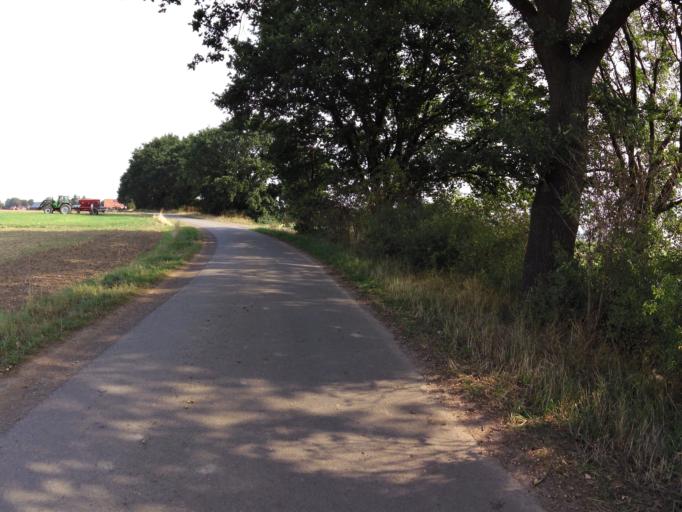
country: DE
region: Lower Saxony
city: Stolzenau
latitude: 52.4836
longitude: 9.0217
